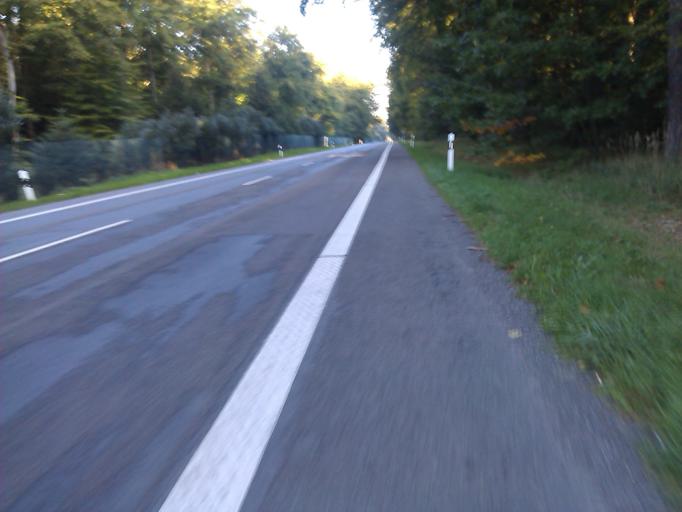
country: DE
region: Hesse
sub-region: Regierungsbezirk Darmstadt
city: Erzhausen
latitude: 49.9784
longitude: 8.6446
